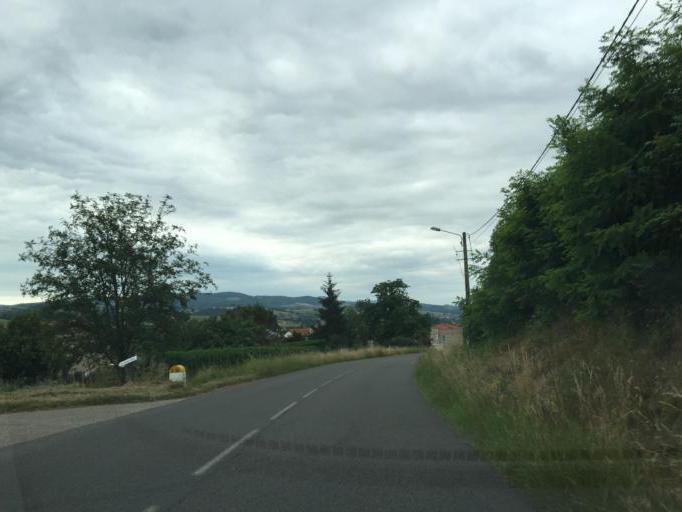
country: FR
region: Rhone-Alpes
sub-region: Departement de la Loire
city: Saint-Jean-Bonnefonds
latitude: 45.4489
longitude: 4.4810
